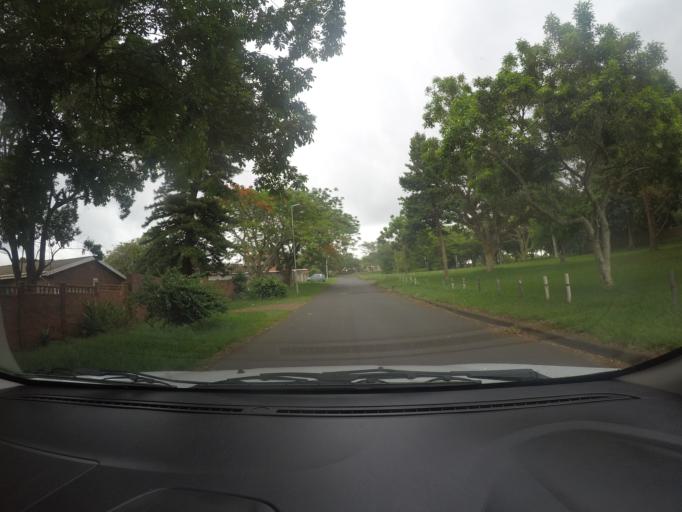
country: ZA
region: KwaZulu-Natal
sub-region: uThungulu District Municipality
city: Empangeni
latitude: -28.7636
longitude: 31.8939
